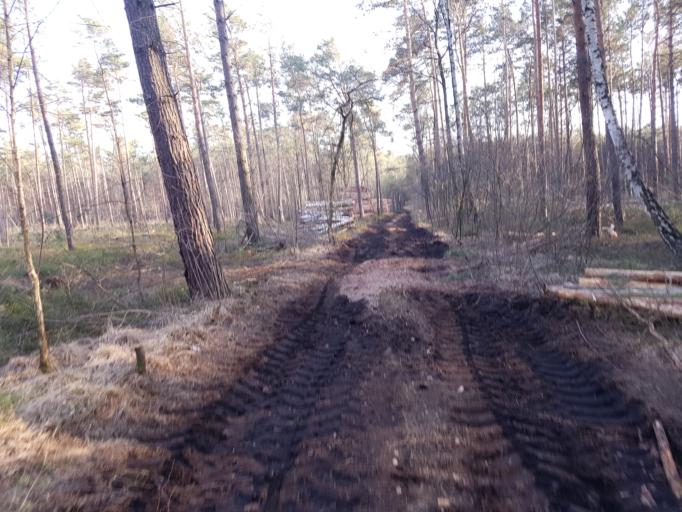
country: DE
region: Brandenburg
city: Schonewalde
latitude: 51.6322
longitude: 13.6162
